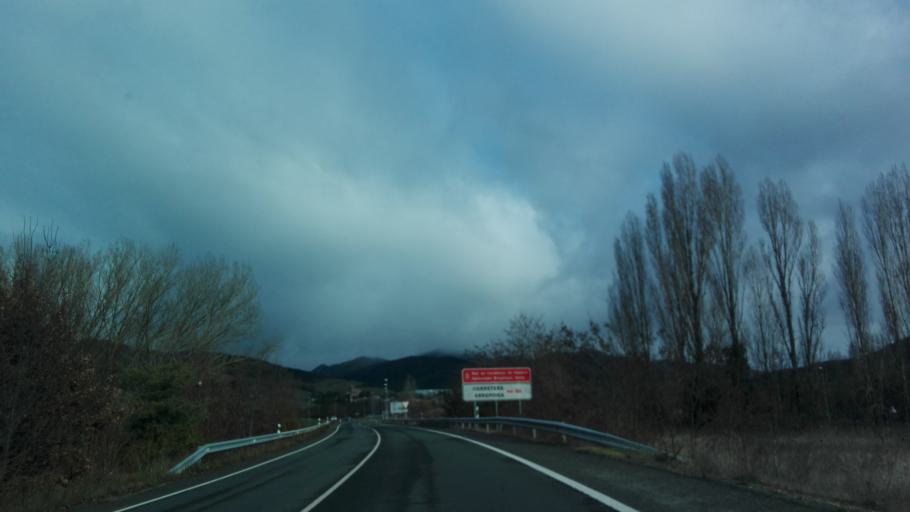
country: ES
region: Navarre
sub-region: Provincia de Navarra
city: Egues-Uharte
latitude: 42.8229
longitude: -1.5500
